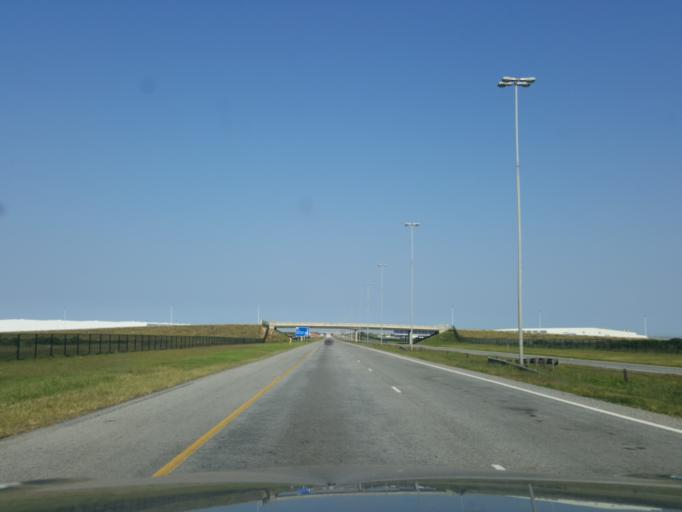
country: ZA
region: Eastern Cape
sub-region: Nelson Mandela Bay Metropolitan Municipality
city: Port Elizabeth
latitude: -33.8100
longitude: 25.6524
